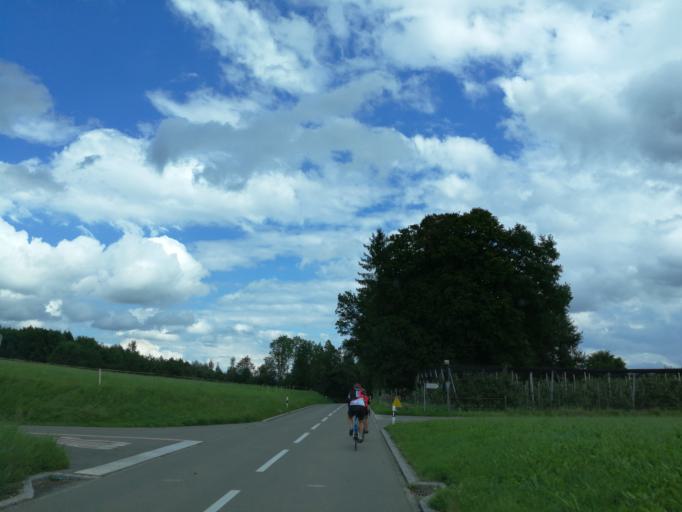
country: CH
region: Thurgau
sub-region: Weinfelden District
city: Sulgen
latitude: 47.5146
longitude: 9.1845
